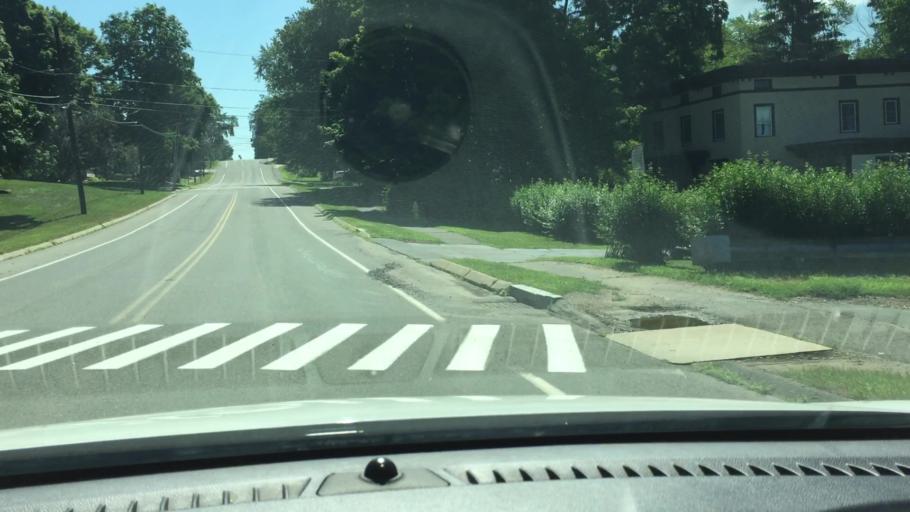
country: US
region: Massachusetts
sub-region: Berkshire County
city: Pittsfield
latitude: 42.4365
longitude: -73.2403
